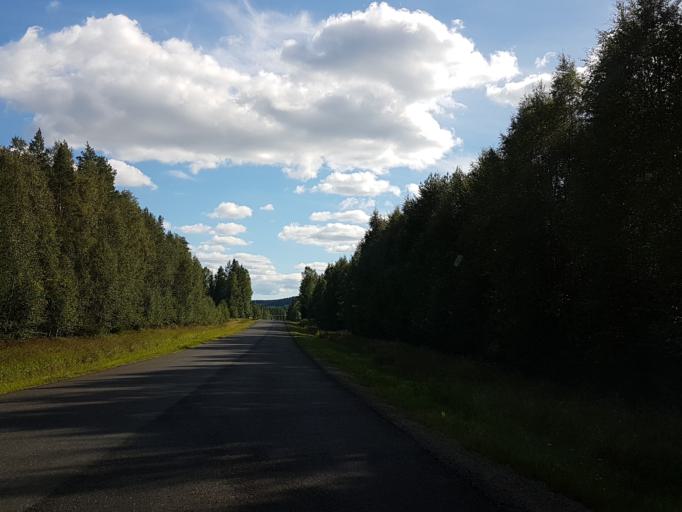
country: SE
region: Vaesterbotten
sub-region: Skelleftea Kommun
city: Burtraesk
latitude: 64.3052
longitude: 20.5278
